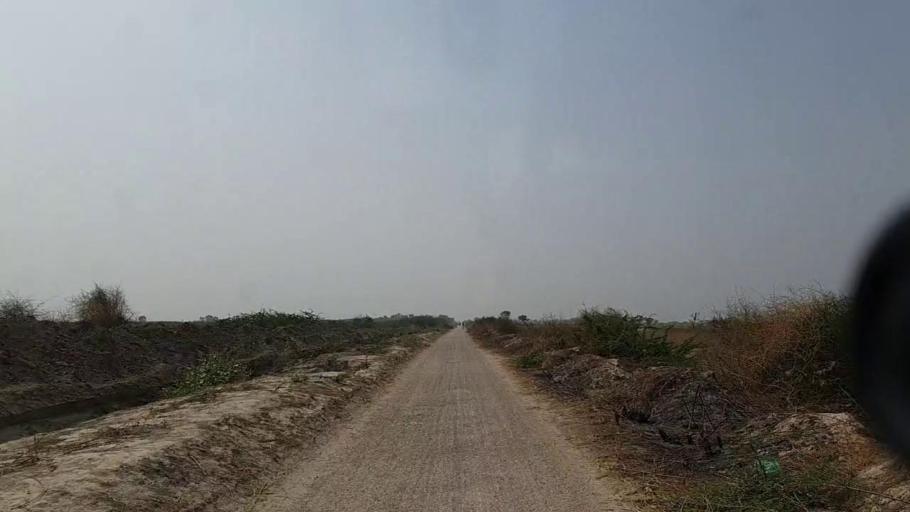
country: PK
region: Sindh
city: Naukot
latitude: 24.7711
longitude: 69.3268
